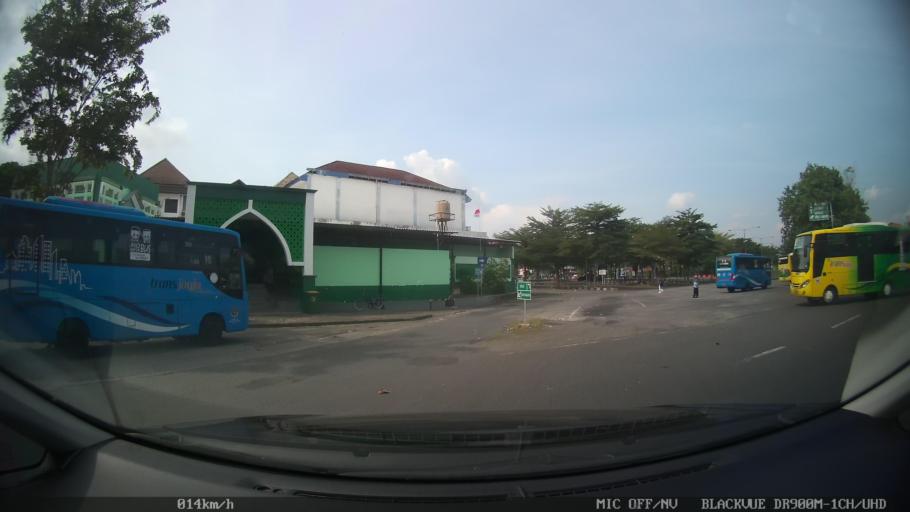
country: ID
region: Daerah Istimewa Yogyakarta
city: Depok
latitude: -7.7846
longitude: 110.4356
